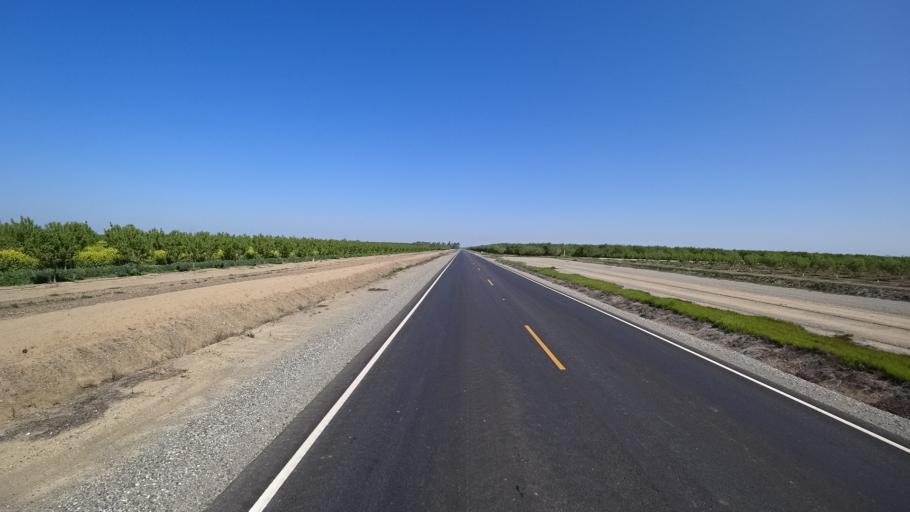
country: US
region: California
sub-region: Glenn County
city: Hamilton City
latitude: 39.6458
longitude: -122.0650
